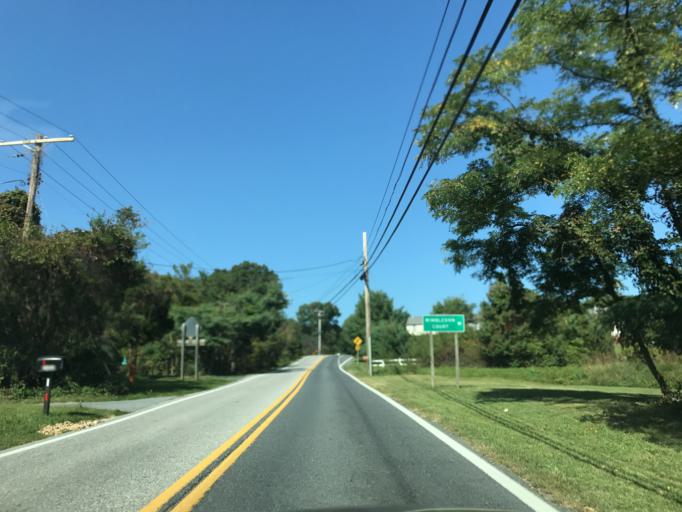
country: US
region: Maryland
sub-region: Anne Arundel County
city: Jessup
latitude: 39.1949
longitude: -76.7778
